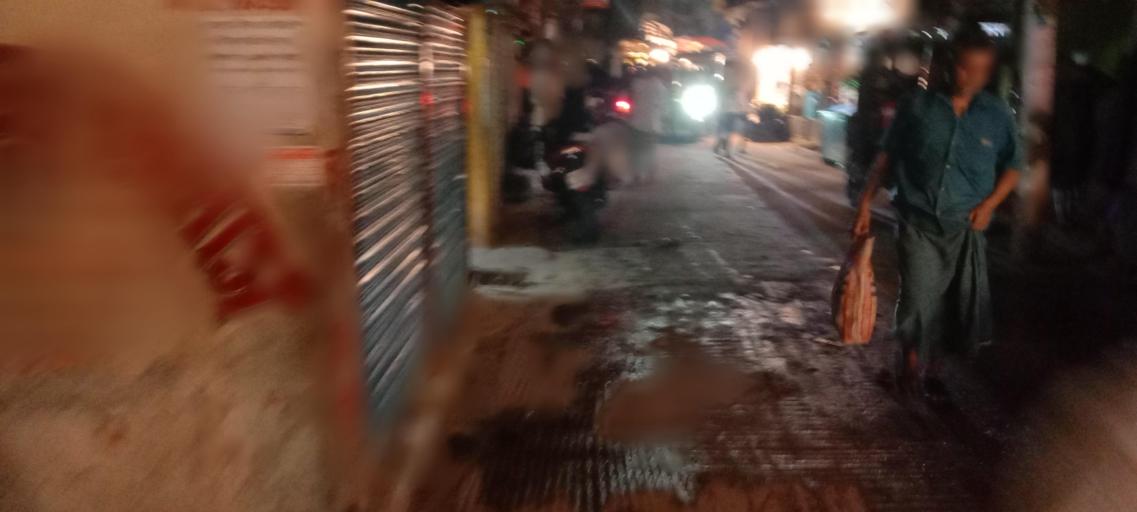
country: BD
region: Dhaka
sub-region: Dhaka
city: Dhaka
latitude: 23.6600
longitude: 90.3600
